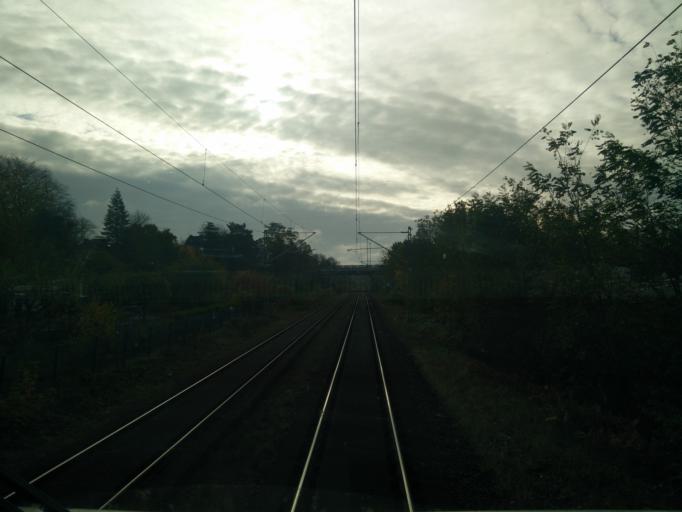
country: DE
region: Berlin
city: Westend
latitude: 52.5177
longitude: 13.2531
